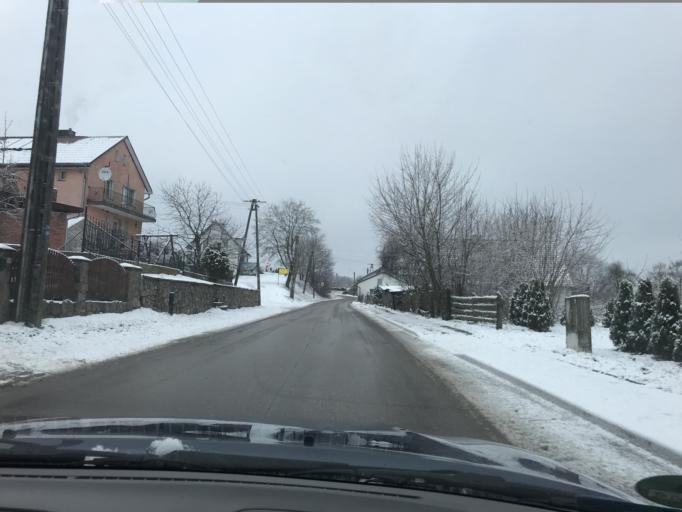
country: PL
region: Pomeranian Voivodeship
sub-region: Powiat bytowski
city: Bytow
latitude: 54.2174
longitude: 17.5618
